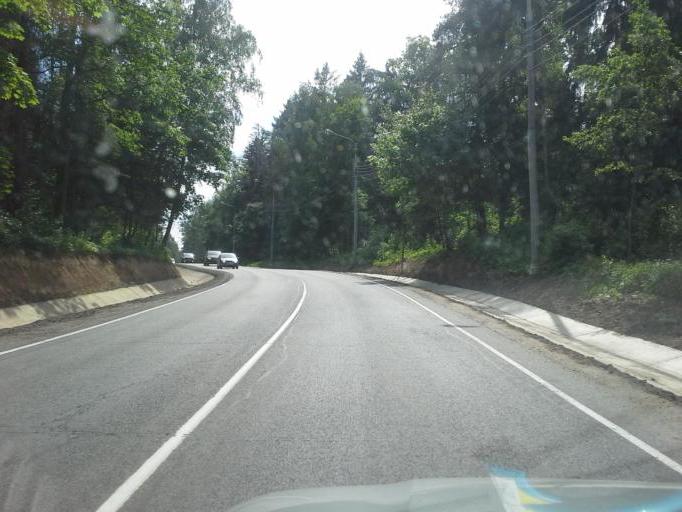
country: RU
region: Moskovskaya
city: Odintsovo
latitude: 55.7056
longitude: 37.2700
